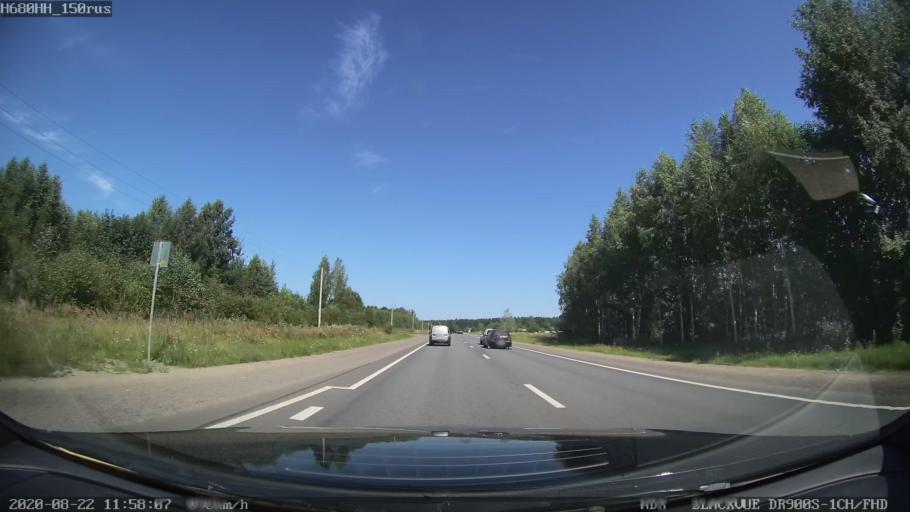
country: RU
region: Tverskaya
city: Rameshki
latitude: 57.1869
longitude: 36.0828
